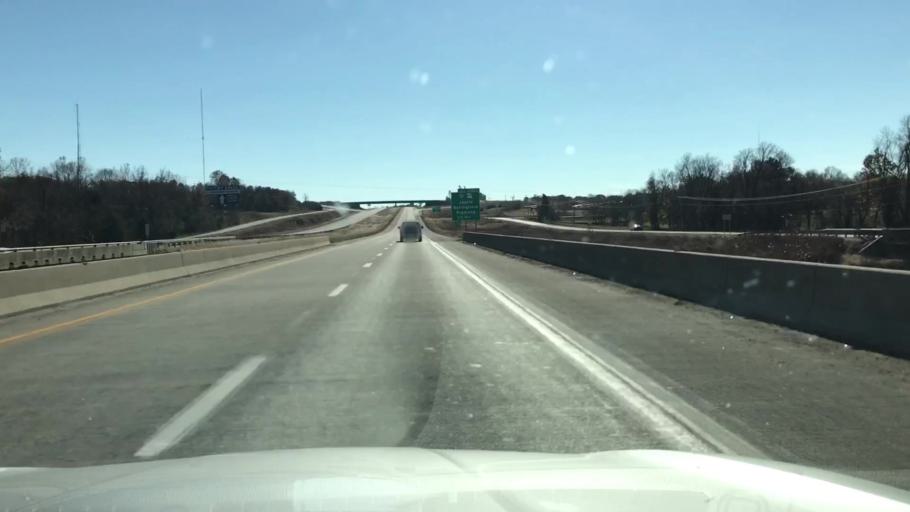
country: US
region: Missouri
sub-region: Jasper County
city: Carthage
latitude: 37.1054
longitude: -94.3105
